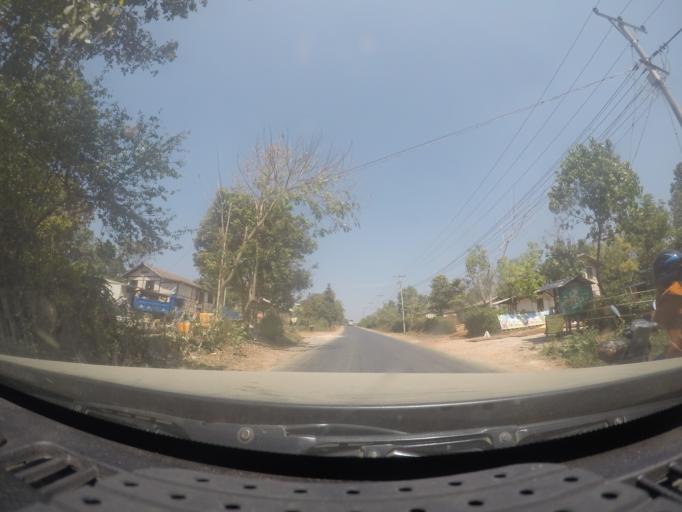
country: MM
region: Shan
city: Taunggyi
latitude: 20.9374
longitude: 96.5472
